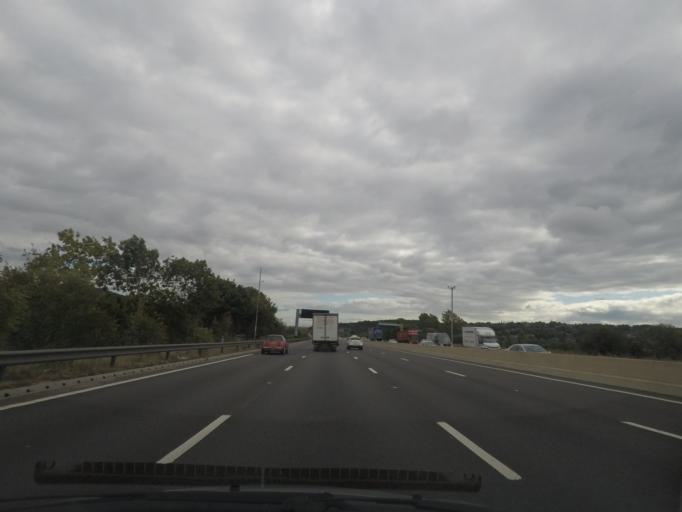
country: GB
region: England
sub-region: Rotherham
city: Wentworth
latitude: 53.4433
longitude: -1.4398
